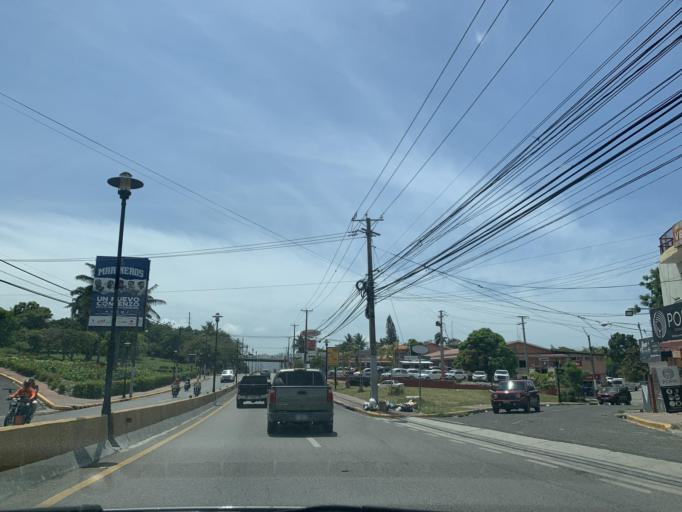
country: DO
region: Puerto Plata
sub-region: Puerto Plata
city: Puerto Plata
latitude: 19.7867
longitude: -70.6899
